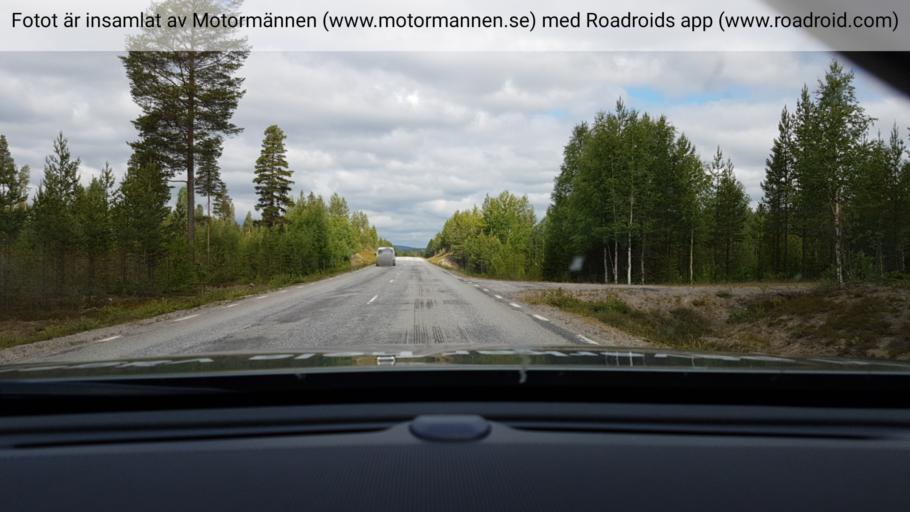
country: SE
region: Vaesterbotten
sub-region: Mala Kommun
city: Mala
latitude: 64.9704
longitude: 18.5804
